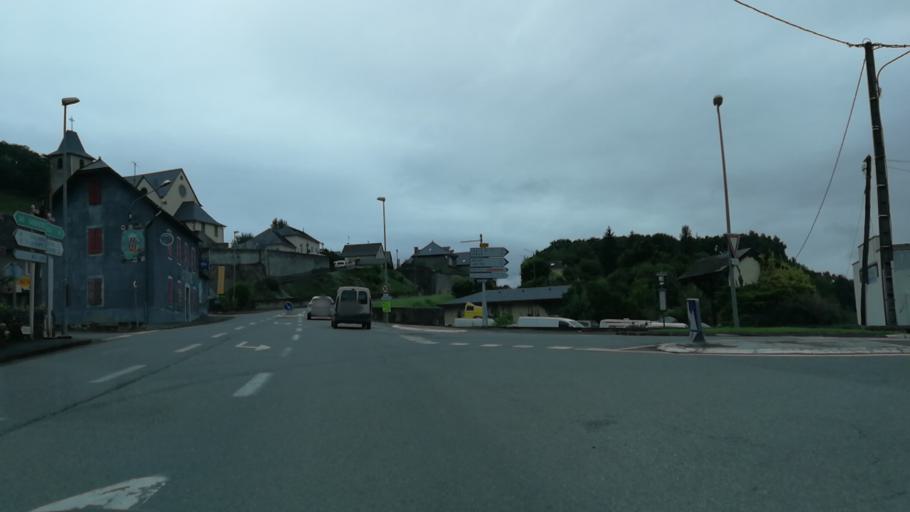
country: FR
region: Aquitaine
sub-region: Departement des Pyrenees-Atlantiques
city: Oloron-Sainte-Marie
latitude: 43.1219
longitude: -0.6136
